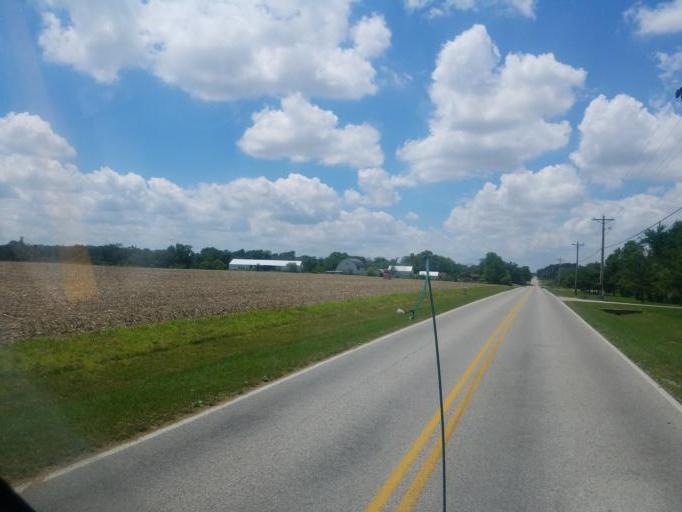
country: US
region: Ohio
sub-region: Huron County
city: Willard
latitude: 41.0793
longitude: -82.7183
